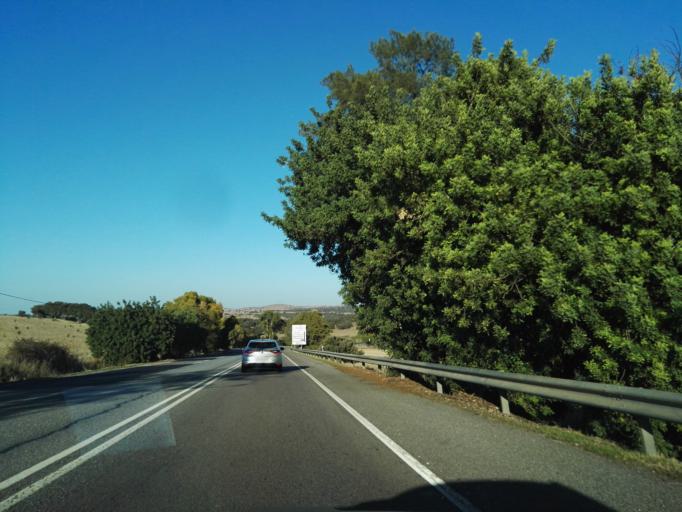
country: PT
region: Evora
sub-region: Vila Vicosa
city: Vila Vicosa
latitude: 38.8508
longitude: -7.3363
